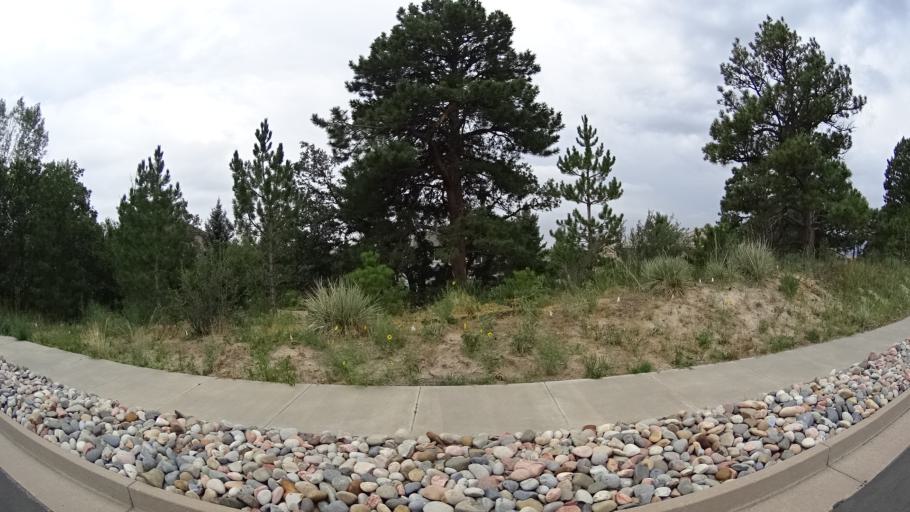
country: US
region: Colorado
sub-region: El Paso County
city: Gleneagle
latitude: 39.0039
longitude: -104.7929
